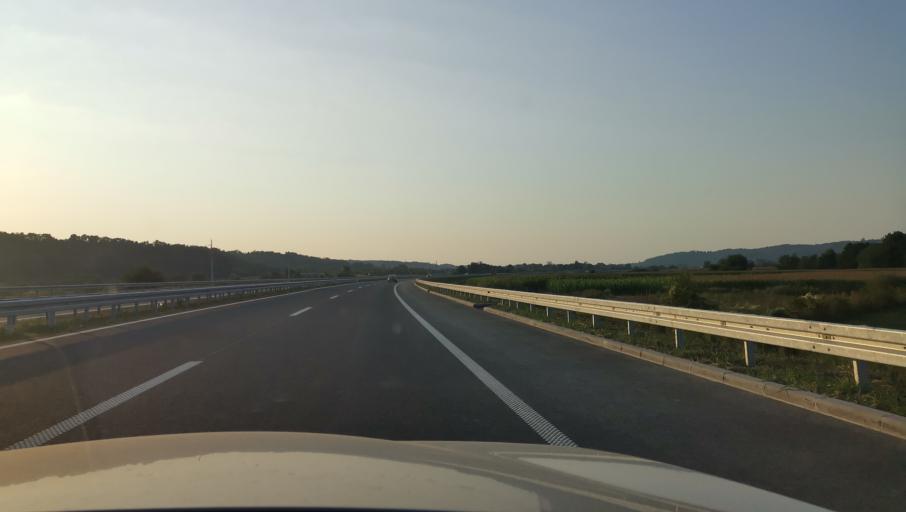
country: RS
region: Central Serbia
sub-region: Kolubarski Okrug
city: Lajkovac
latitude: 44.3112
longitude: 20.2200
